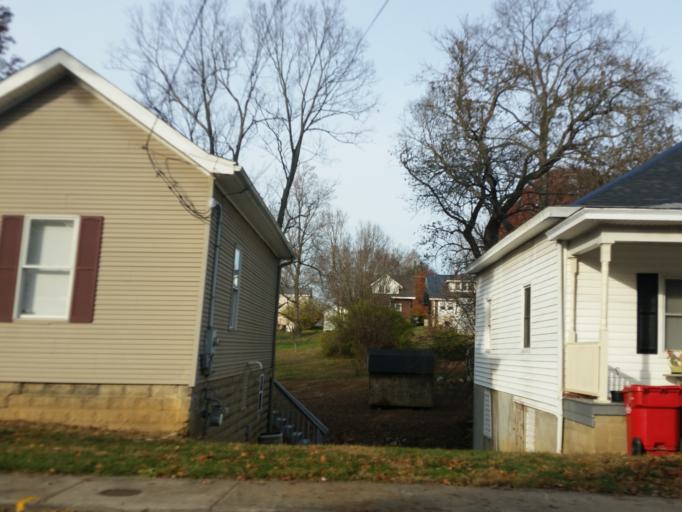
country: US
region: Kentucky
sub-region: Harrison County
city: Cynthiana
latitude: 38.3871
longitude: -84.2872
